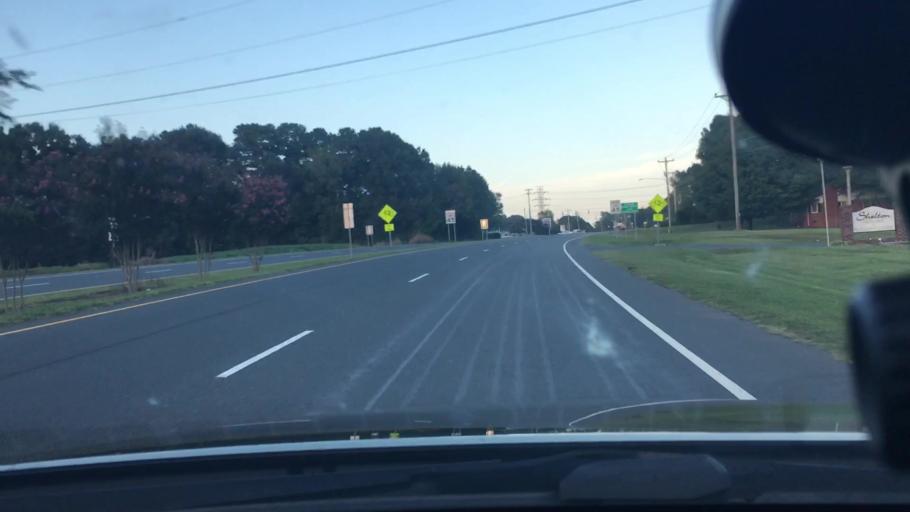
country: US
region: North Carolina
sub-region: Stanly County
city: Albemarle
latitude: 35.3340
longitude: -80.2302
